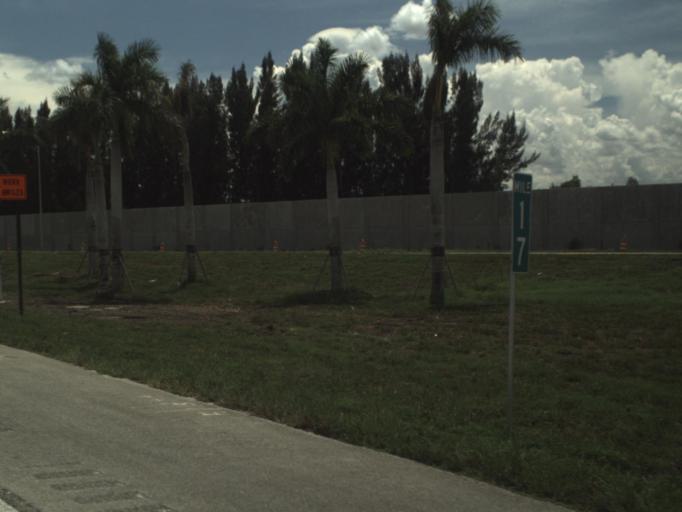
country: US
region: Florida
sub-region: Broward County
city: Weston
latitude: 26.1134
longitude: -80.3522
